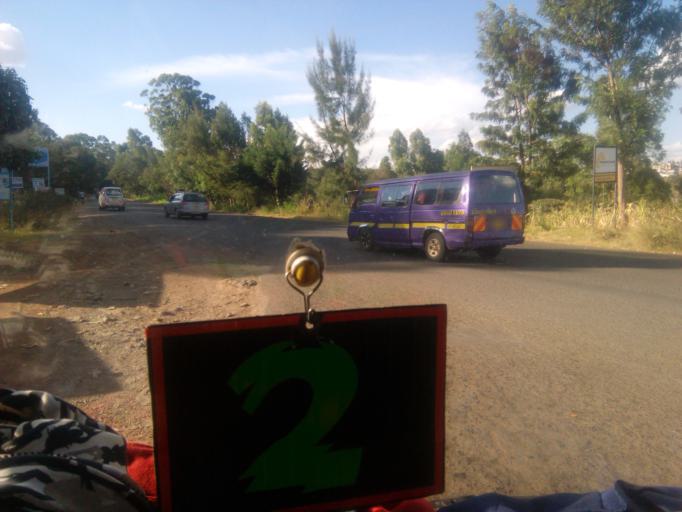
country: KE
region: Kiambu
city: Kikuyu
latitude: -1.2627
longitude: 36.6695
